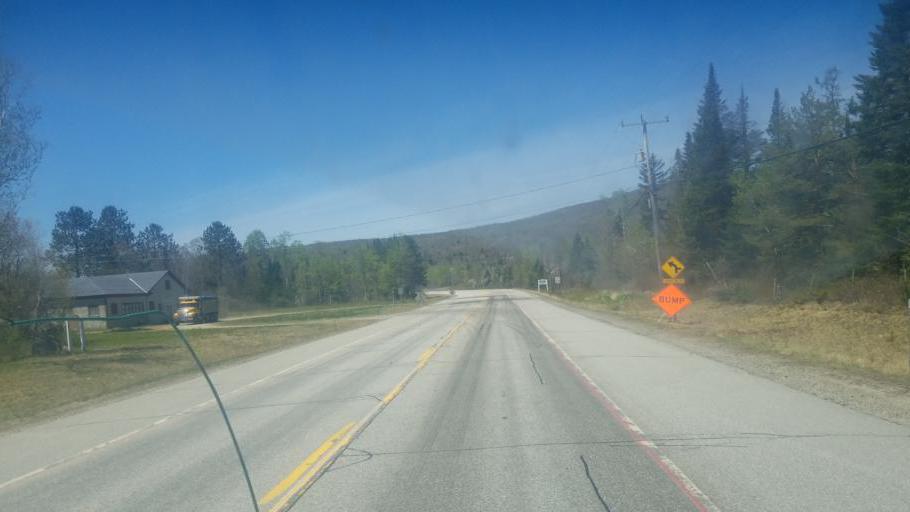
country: US
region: New Hampshire
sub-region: Coos County
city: Jefferson
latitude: 44.2680
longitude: -71.4675
